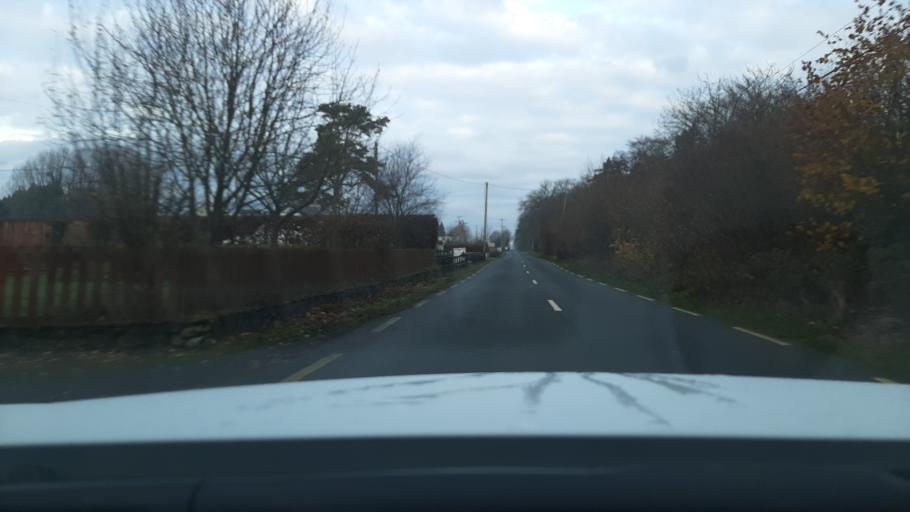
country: IE
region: Leinster
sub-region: Kildare
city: Rathangan
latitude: 53.2383
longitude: -7.0105
